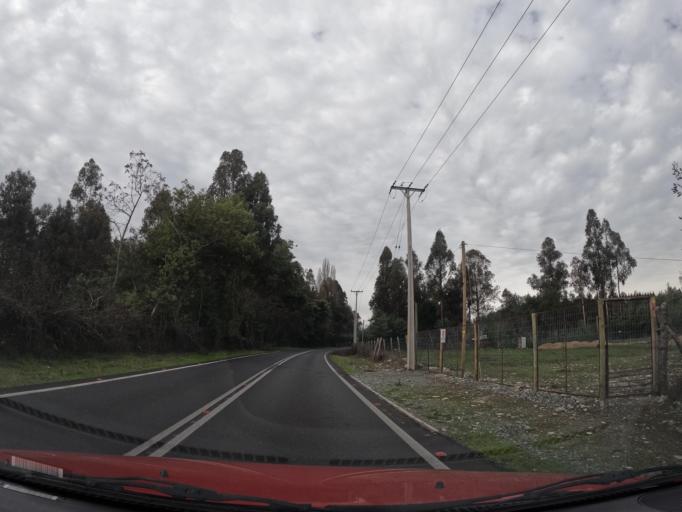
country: CL
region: Maule
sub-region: Provincia de Linares
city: Linares
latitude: -35.9118
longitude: -71.4889
